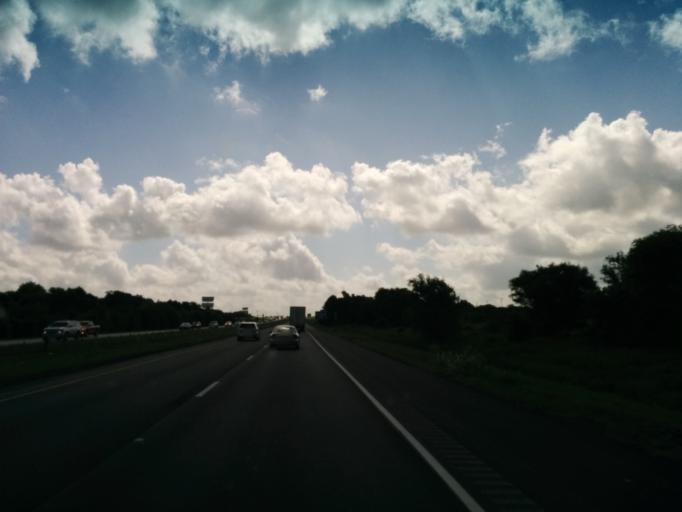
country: US
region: Texas
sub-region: Colorado County
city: Weimar
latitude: 29.6903
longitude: -96.7952
